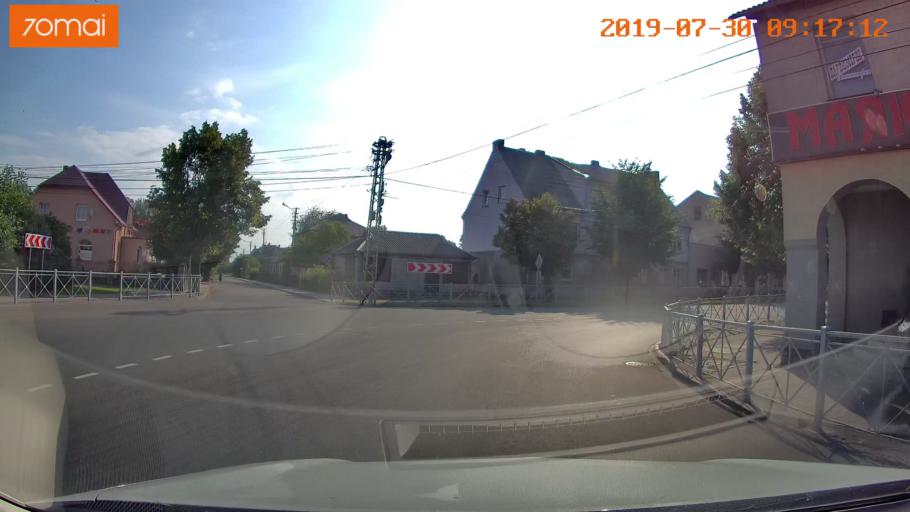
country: RU
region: Kaliningrad
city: Nesterov
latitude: 54.6347
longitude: 22.5671
